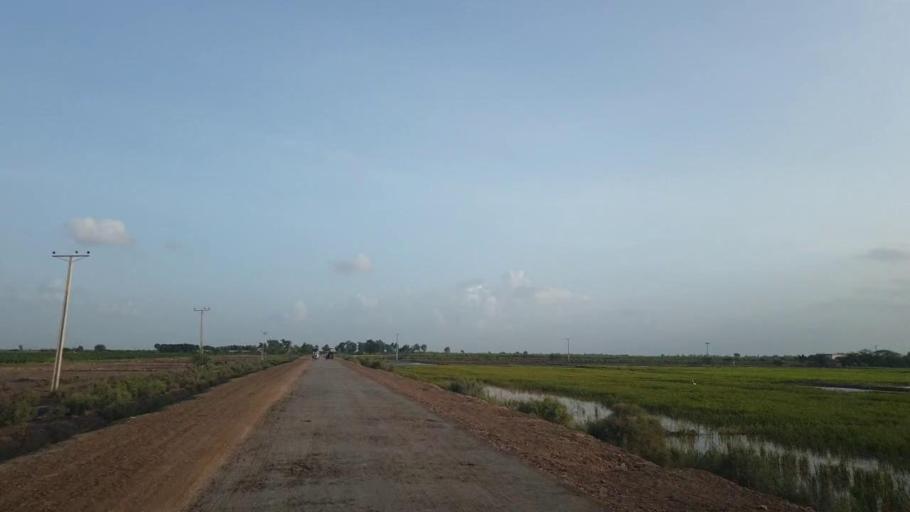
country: PK
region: Sindh
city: Kadhan
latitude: 24.6219
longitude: 69.1158
